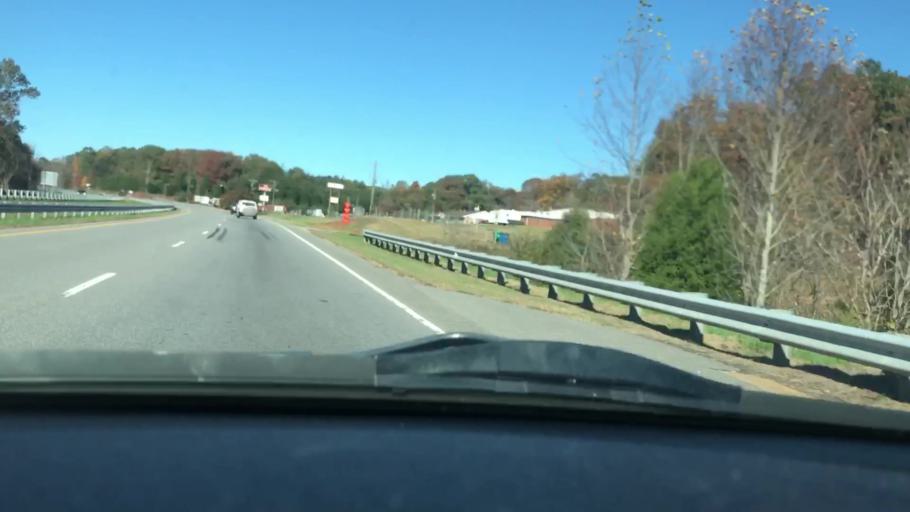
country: US
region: North Carolina
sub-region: Rockingham County
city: Stoneville
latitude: 36.4771
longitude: -79.9244
